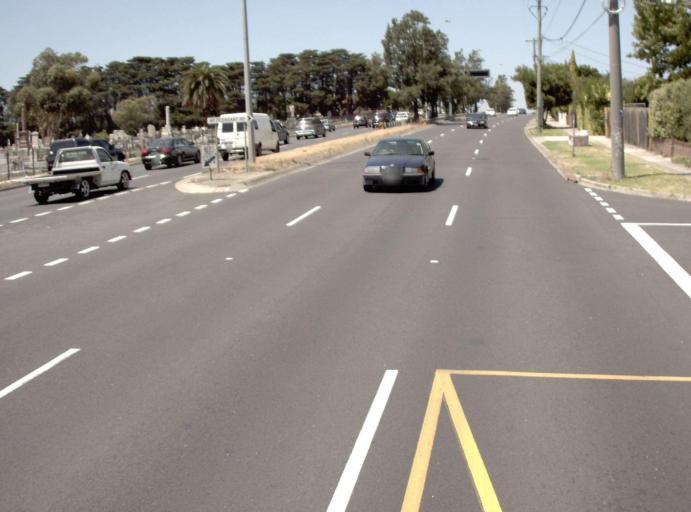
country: AU
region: Victoria
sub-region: Moreland
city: Coburg
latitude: -37.7431
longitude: 144.9824
